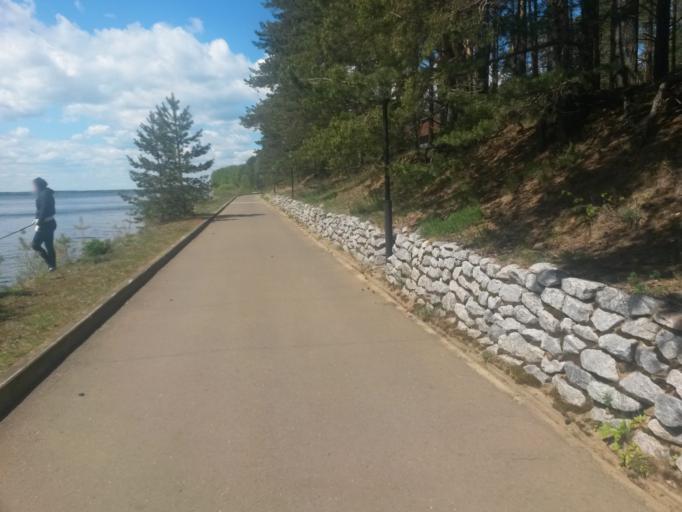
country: RU
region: Jaroslavl
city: Borok
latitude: 58.0617
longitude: 38.3490
